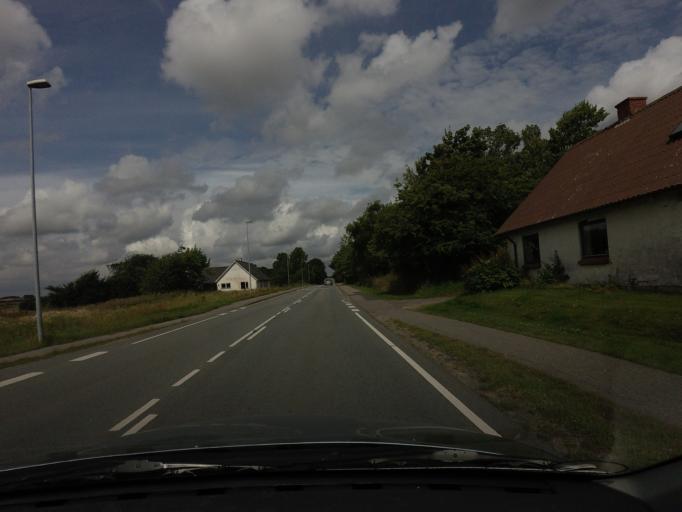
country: DK
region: North Denmark
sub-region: Hjorring Kommune
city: Tars
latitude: 57.3634
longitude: 10.1951
